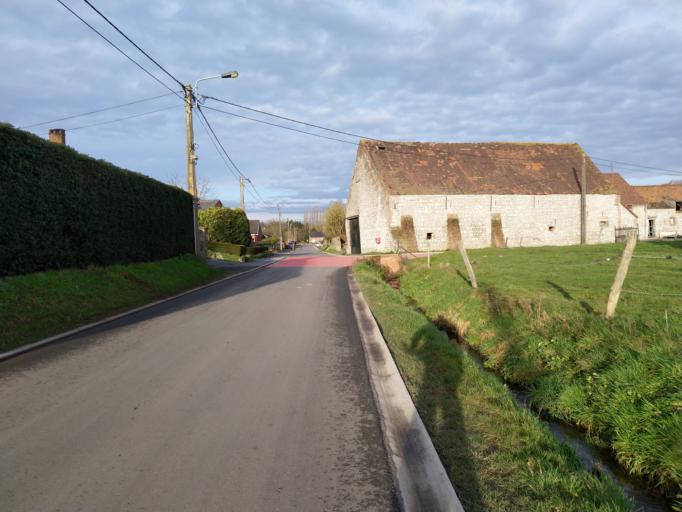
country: BE
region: Wallonia
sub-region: Province du Hainaut
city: Mons
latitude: 50.5179
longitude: 4.0000
